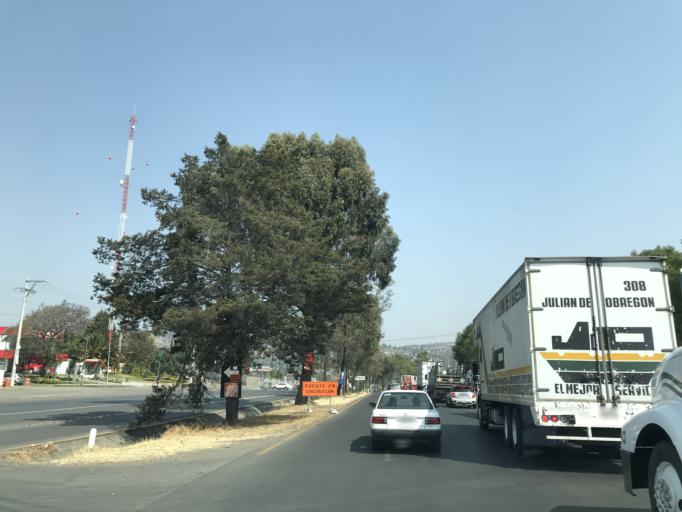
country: MX
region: Tlaxcala
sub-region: Apetatitlan de Antonio Carvajal
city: Tlatempan
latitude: 19.3352
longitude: -98.1978
